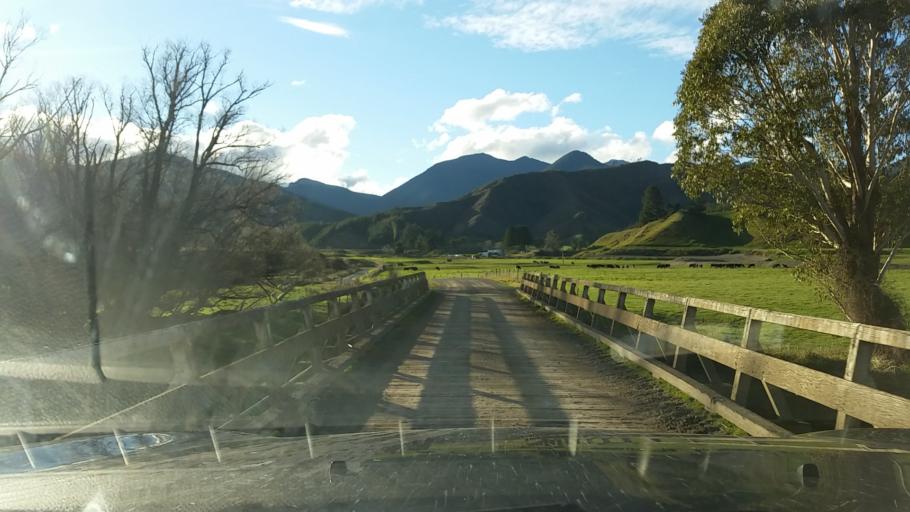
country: NZ
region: Nelson
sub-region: Nelson City
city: Nelson
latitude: -41.5442
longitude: 173.4977
